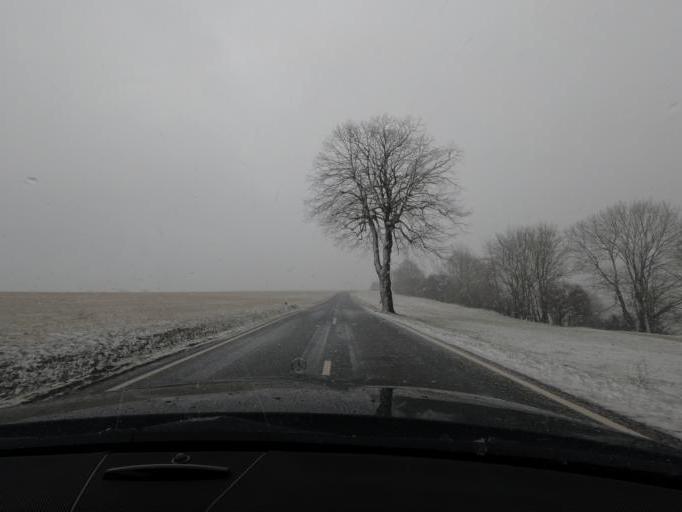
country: DE
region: Thuringia
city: Effelder
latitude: 51.2348
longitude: 10.2615
